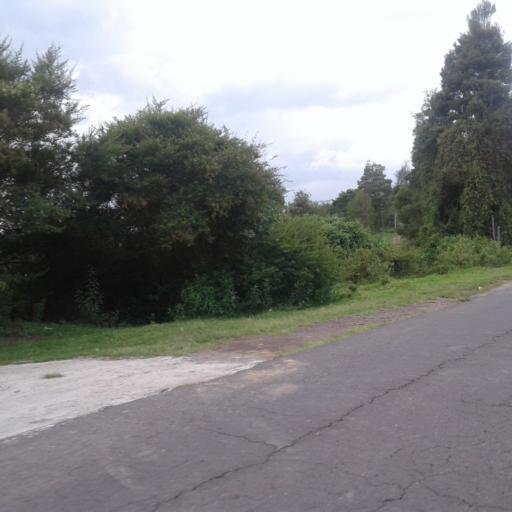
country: EC
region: Pichincha
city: Sangolqui
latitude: -0.2926
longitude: -78.3920
